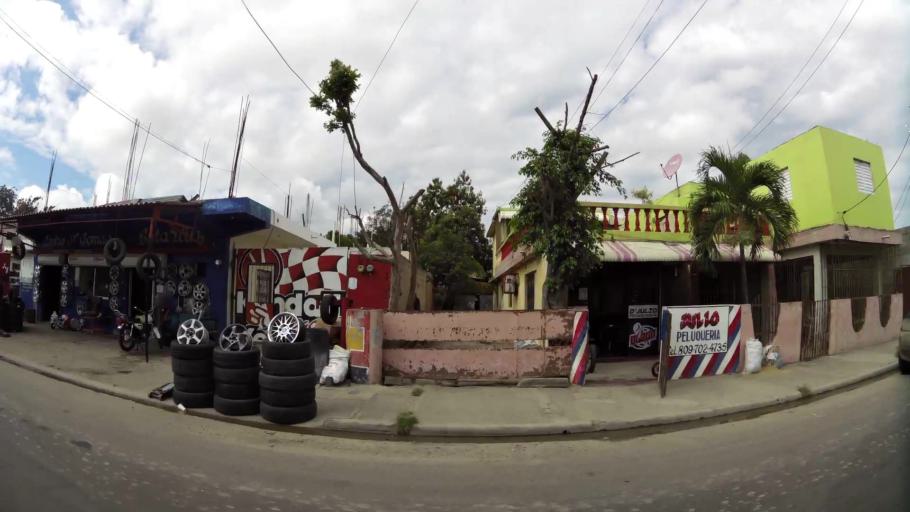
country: DO
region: Santiago
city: Santiago de los Caballeros
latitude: 19.4395
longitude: -70.7061
